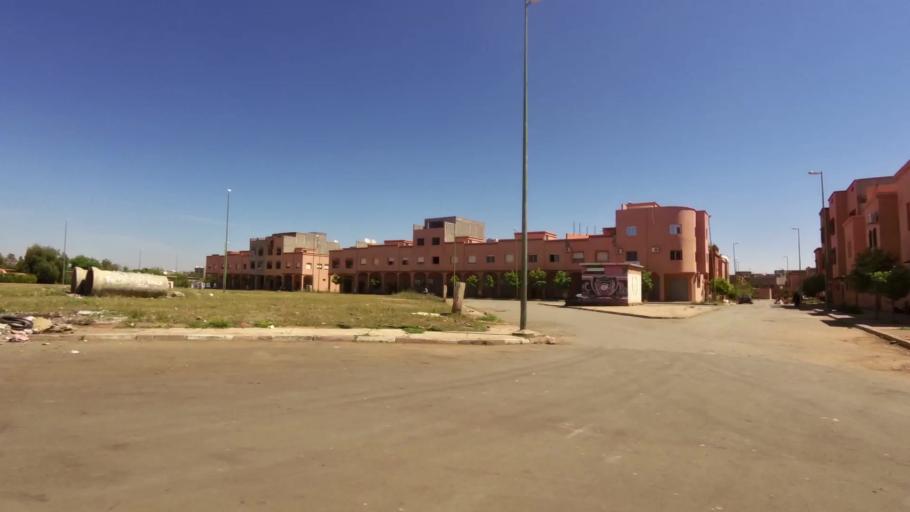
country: MA
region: Marrakech-Tensift-Al Haouz
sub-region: Marrakech
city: Marrakesh
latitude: 31.5730
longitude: -7.9848
